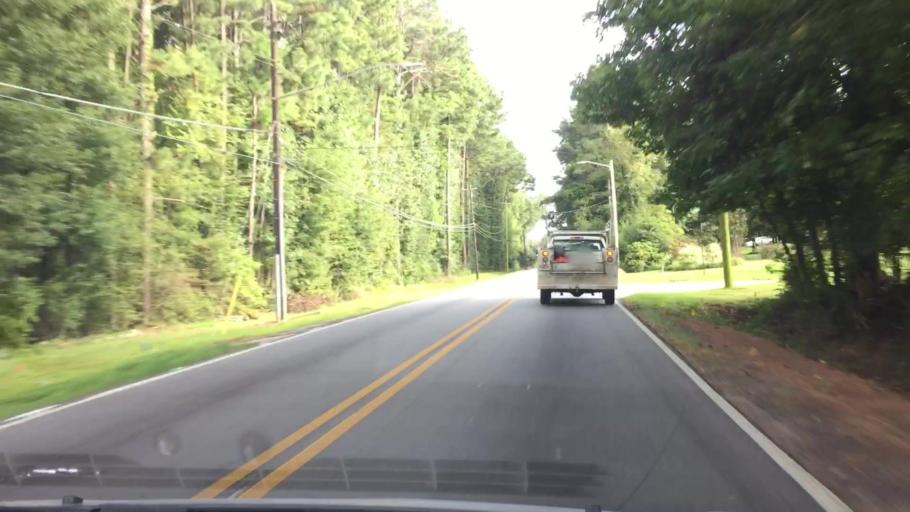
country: US
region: Georgia
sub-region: Clayton County
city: Conley
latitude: 33.6555
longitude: -84.2860
